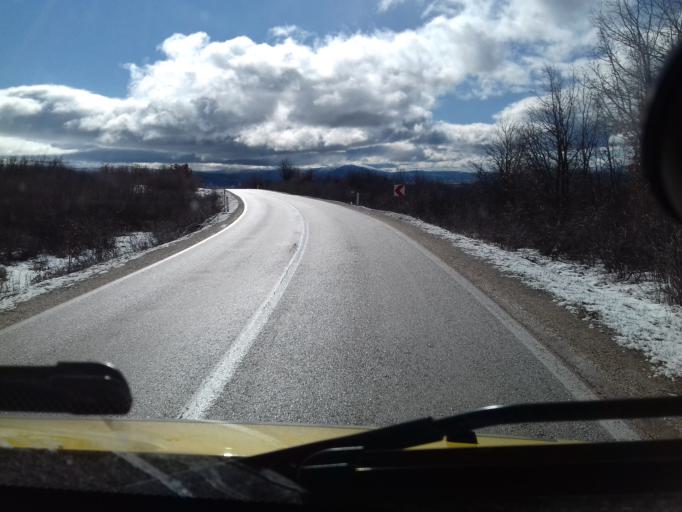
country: BA
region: Federation of Bosnia and Herzegovina
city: Tomislavgrad
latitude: 43.7820
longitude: 17.2223
